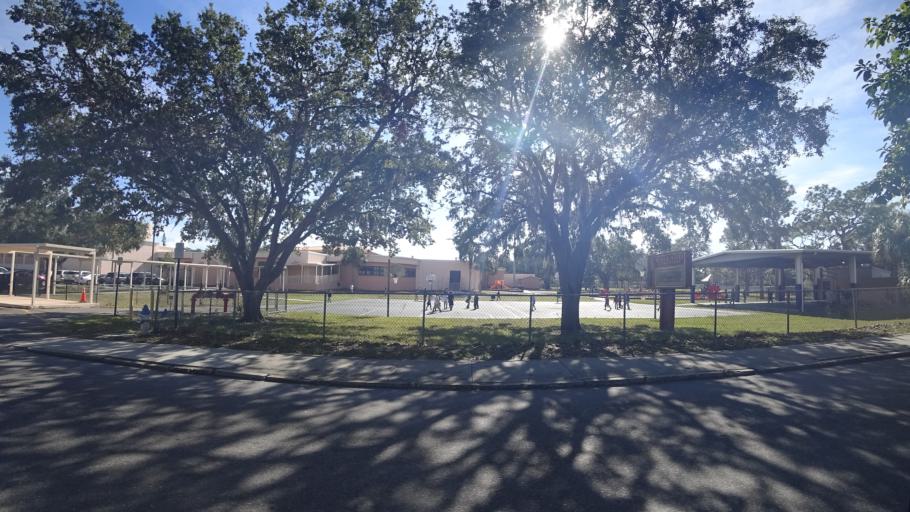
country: US
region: Florida
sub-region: Manatee County
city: Bradenton
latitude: 27.4919
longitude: -82.5805
